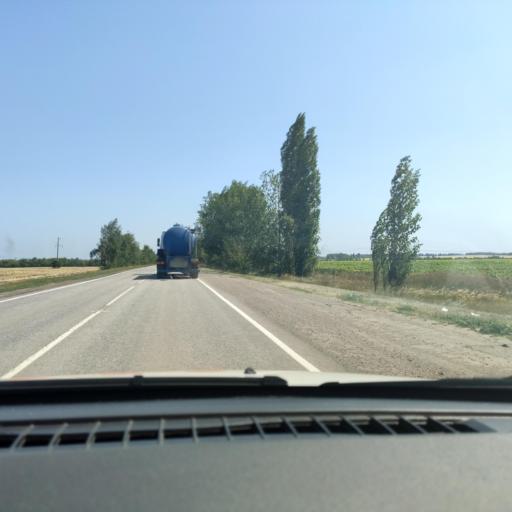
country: RU
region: Voronezj
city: Ostrogozhsk
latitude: 50.8116
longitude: 39.2613
